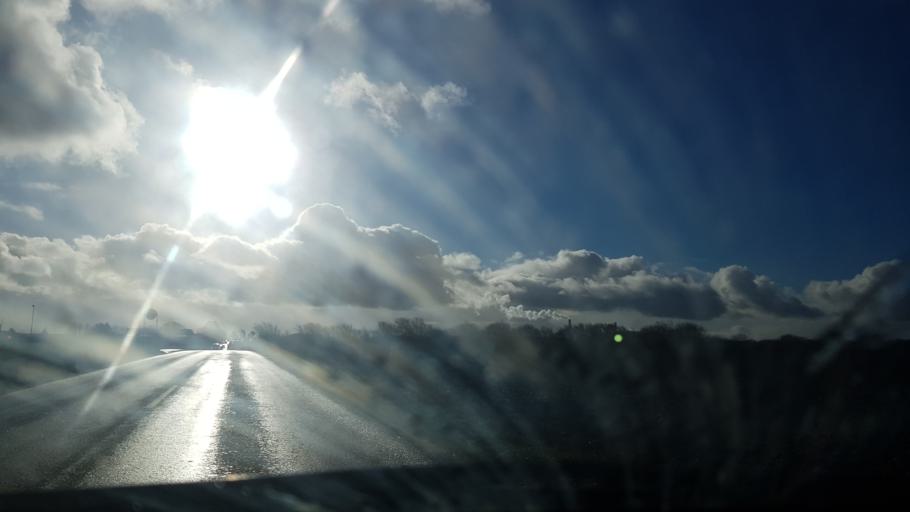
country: DK
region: South Denmark
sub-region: Fredericia Kommune
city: Taulov
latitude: 55.5244
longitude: 9.6380
